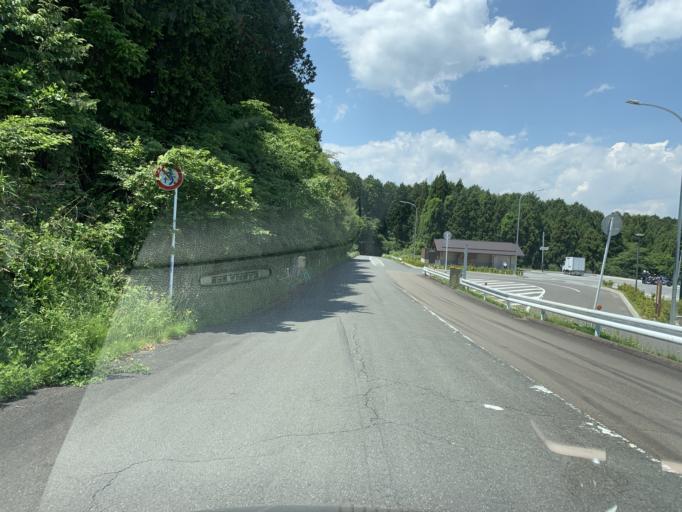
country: JP
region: Miyagi
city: Matsushima
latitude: 38.3669
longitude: 141.0520
